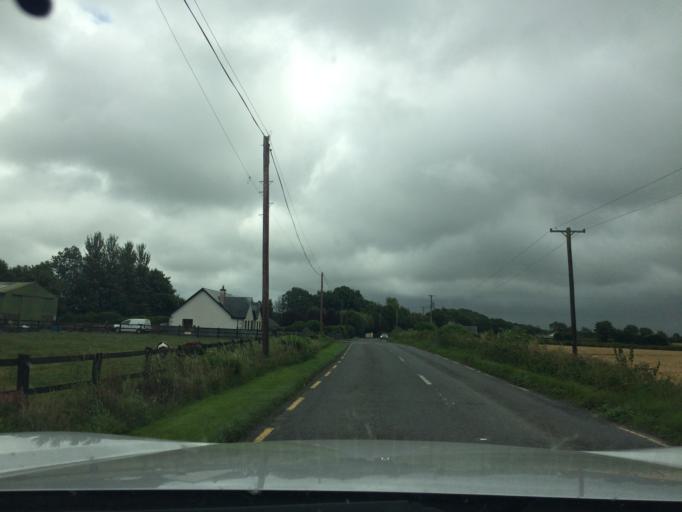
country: IE
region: Munster
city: Cashel
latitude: 52.4838
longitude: -7.8535
